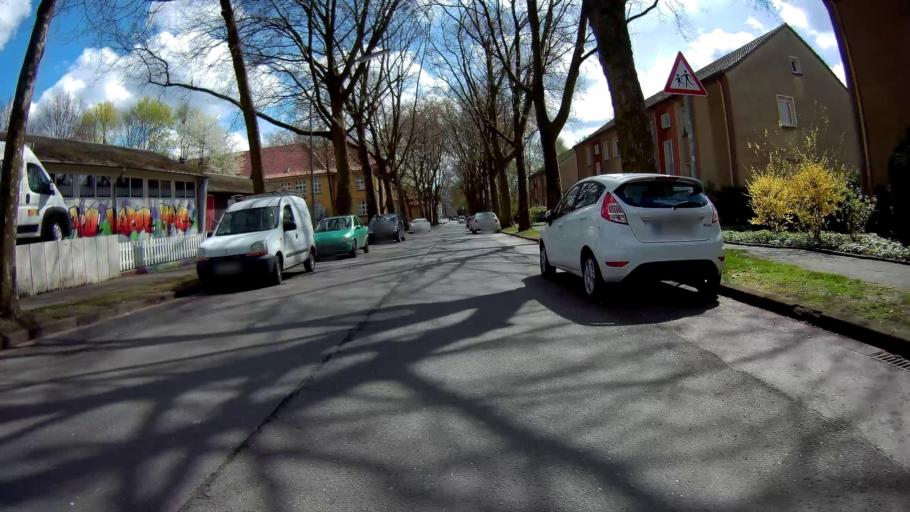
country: DE
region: North Rhine-Westphalia
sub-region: Regierungsbezirk Munster
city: Gladbeck
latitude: 51.5727
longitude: 7.0385
